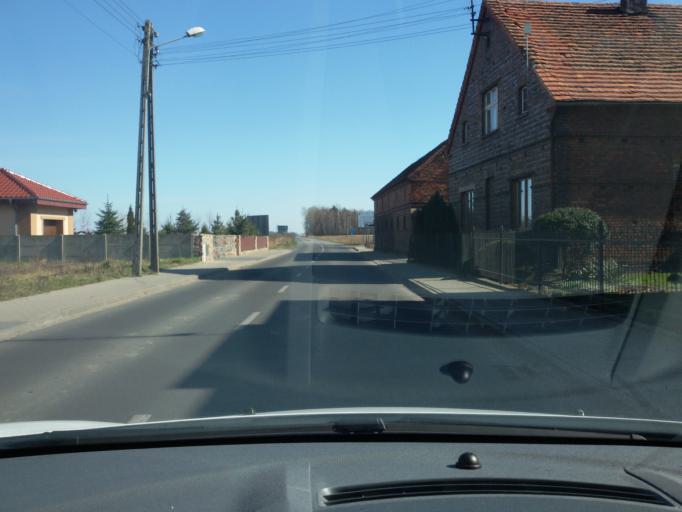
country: PL
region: Greater Poland Voivodeship
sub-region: Powiat rawicki
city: Bojanowo
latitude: 51.7698
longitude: 16.7320
